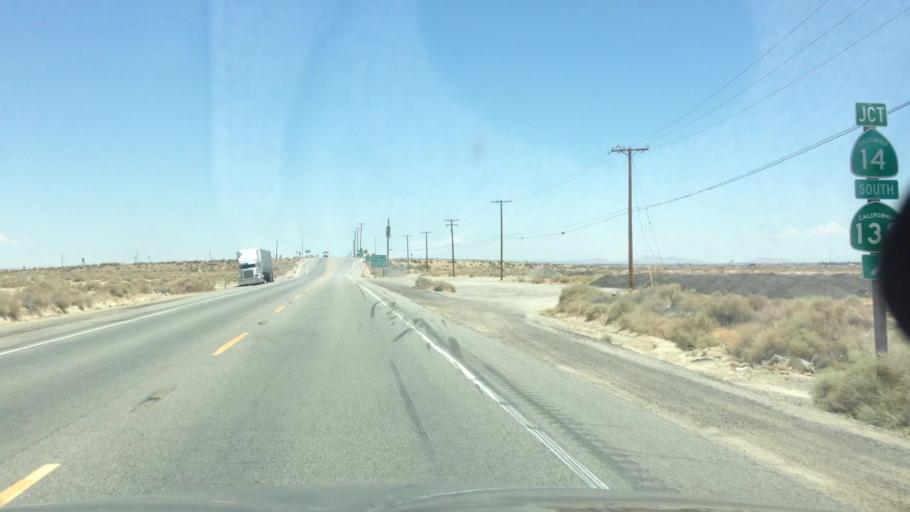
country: US
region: California
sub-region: Los Angeles County
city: Lancaster
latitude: 34.7769
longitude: -118.1761
